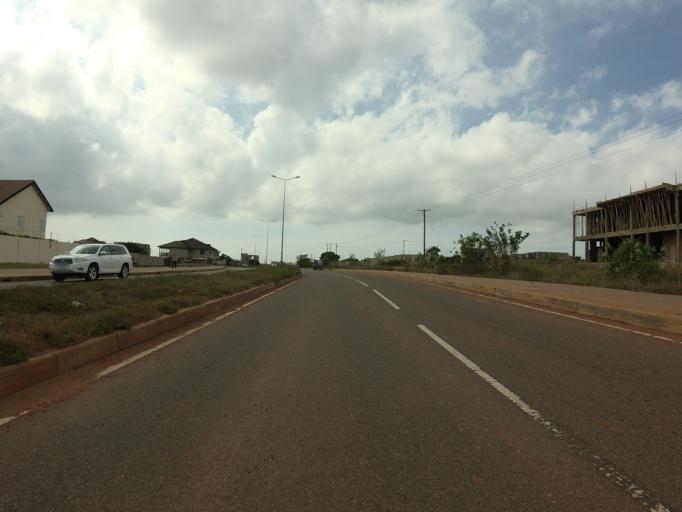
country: GH
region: Greater Accra
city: Teshi Old Town
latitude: 5.6070
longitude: -0.1399
